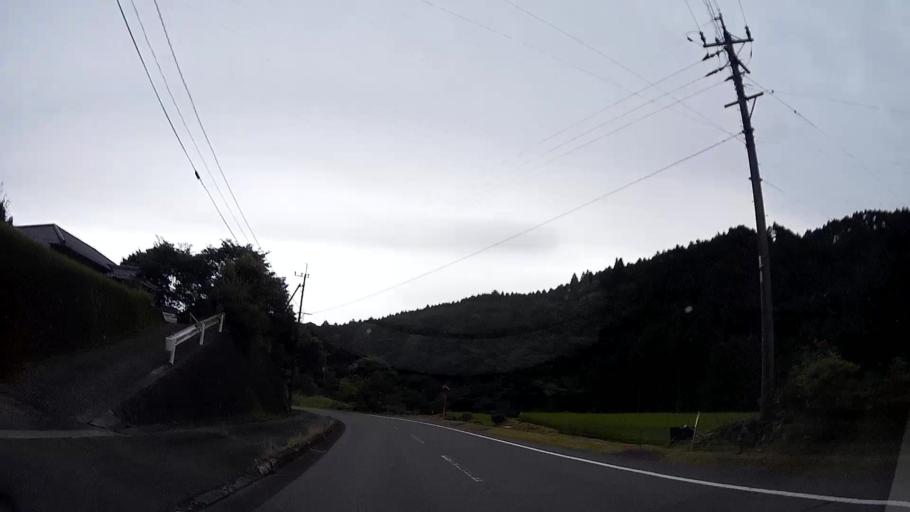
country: JP
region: Kumamoto
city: Kikuchi
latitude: 33.0708
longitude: 130.9099
